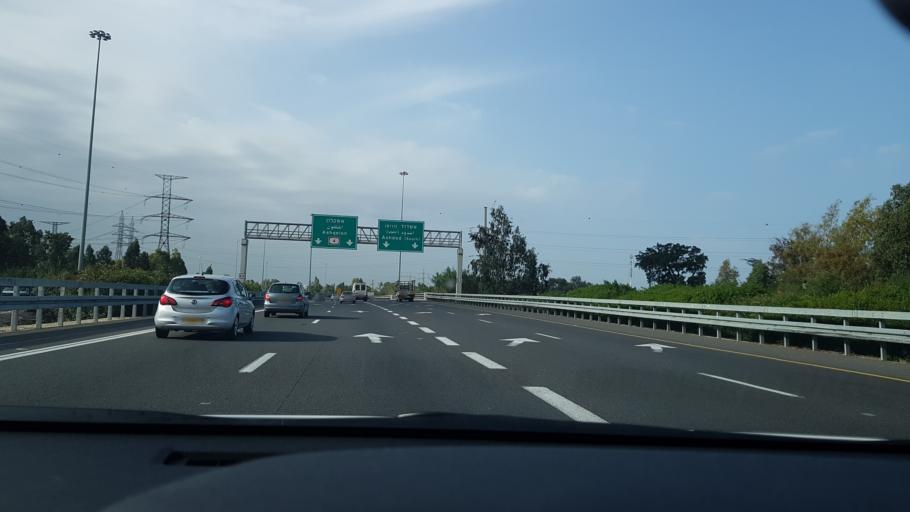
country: IL
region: Southern District
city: Ashdod
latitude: 31.7825
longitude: 34.6710
